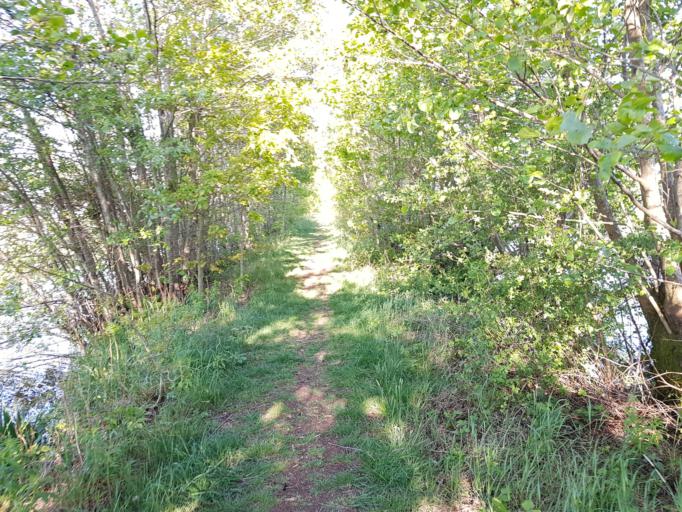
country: NL
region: Utrecht
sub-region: Gemeente Lopik
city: Lopik
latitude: 51.9888
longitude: 4.9223
